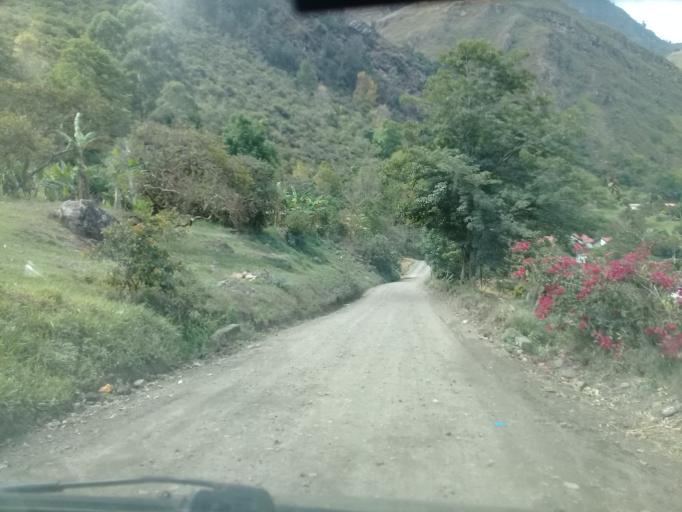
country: CO
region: Cundinamarca
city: Caqueza
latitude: 4.4167
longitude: -73.9847
